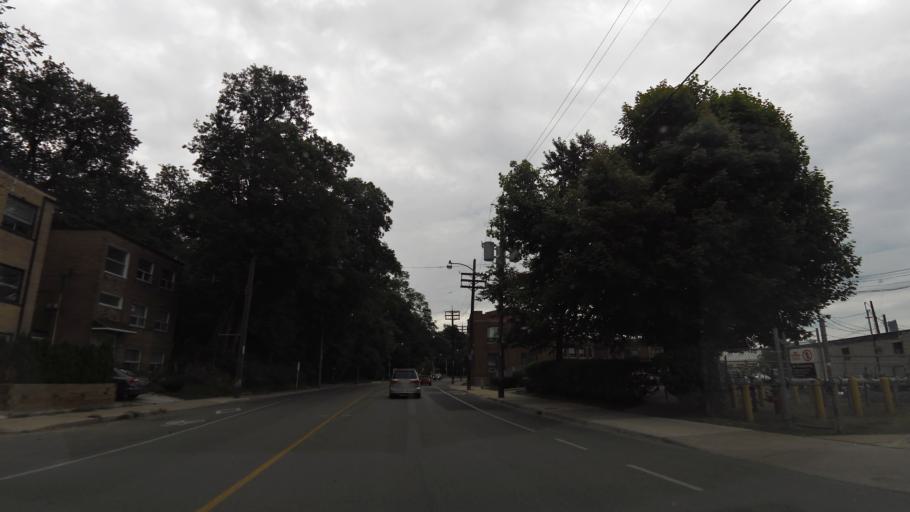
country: CA
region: Ontario
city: Toronto
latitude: 43.6764
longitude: -79.4200
